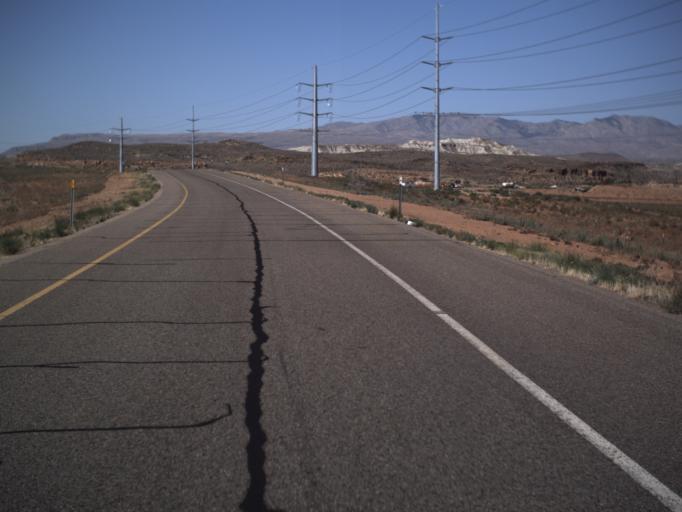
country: US
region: Utah
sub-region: Washington County
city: Washington
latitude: 37.0100
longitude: -113.5085
